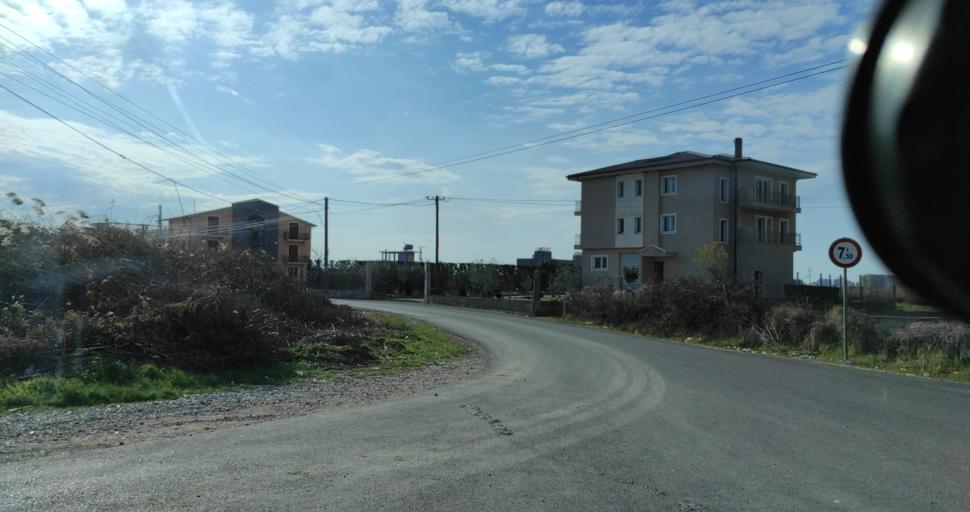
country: AL
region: Lezhe
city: Lezhe
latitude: 41.7860
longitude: 19.6278
